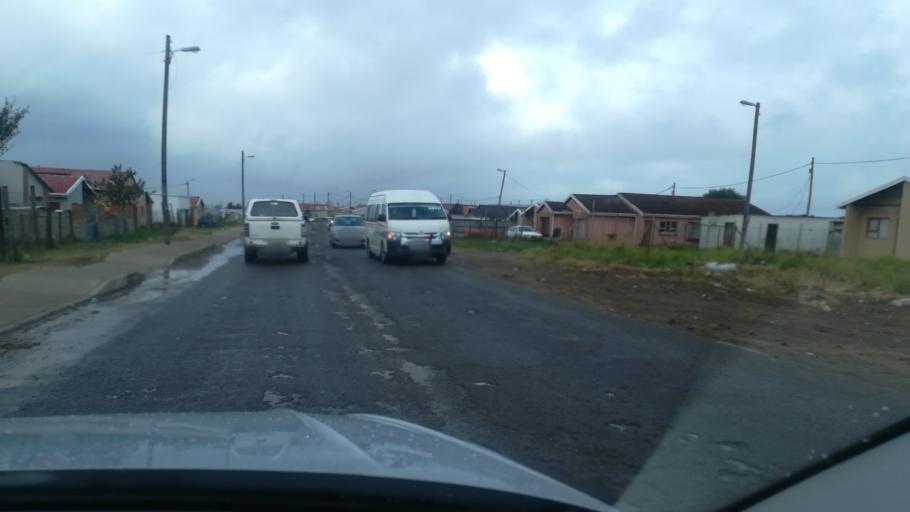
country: ZA
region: Eastern Cape
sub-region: Buffalo City Metropolitan Municipality
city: East London
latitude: -33.0003
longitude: 27.8335
